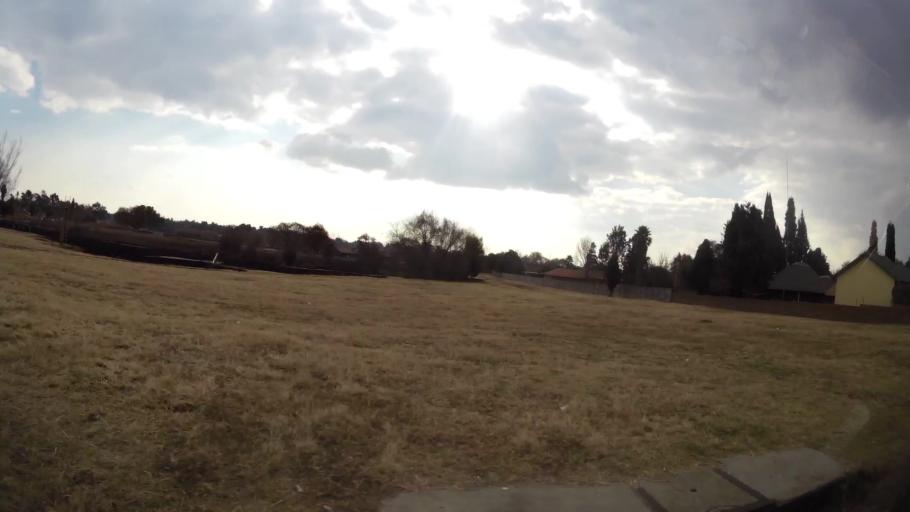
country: ZA
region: Gauteng
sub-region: Ekurhuleni Metropolitan Municipality
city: Benoni
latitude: -26.1196
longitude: 28.3681
